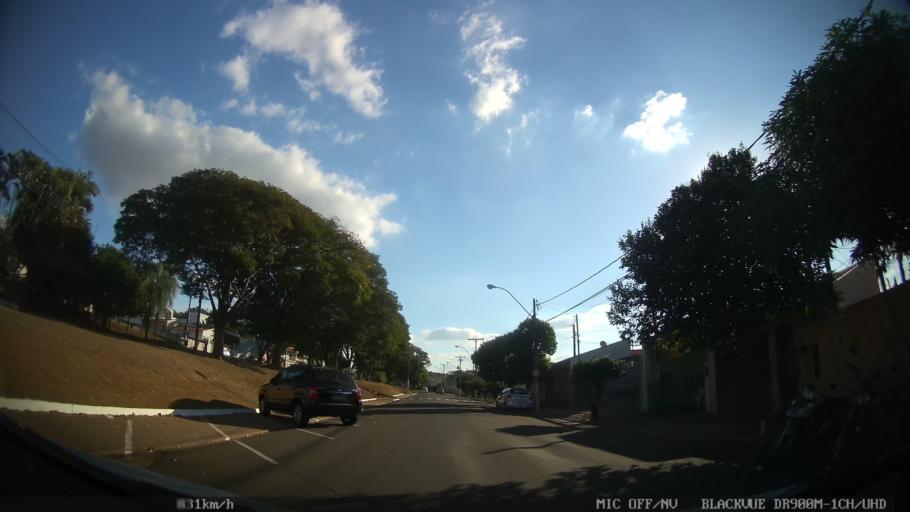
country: BR
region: Sao Paulo
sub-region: Santa Barbara D'Oeste
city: Santa Barbara d'Oeste
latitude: -22.7499
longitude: -47.4226
